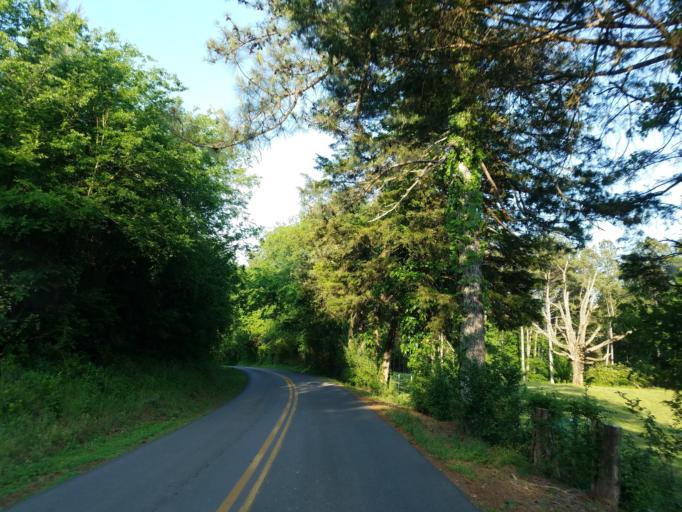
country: US
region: Georgia
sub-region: Gordon County
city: Calhoun
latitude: 34.5253
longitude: -85.1188
